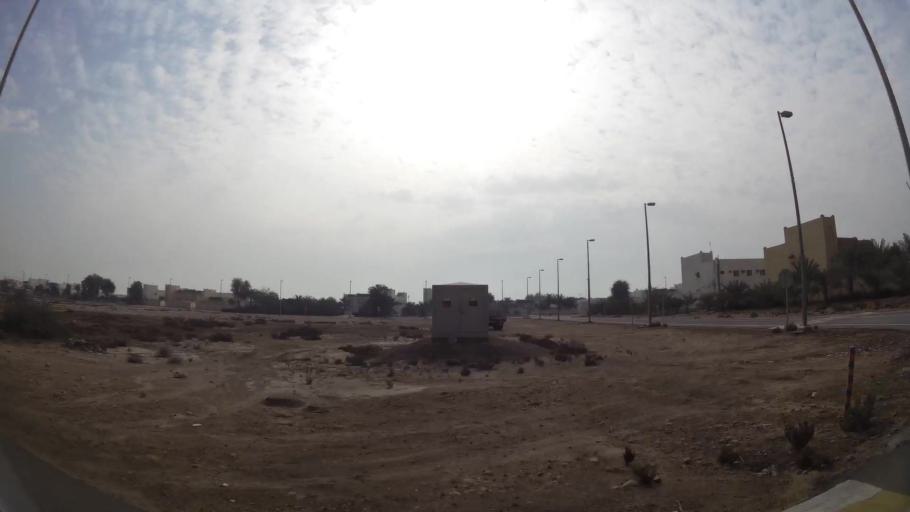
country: AE
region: Abu Dhabi
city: Abu Dhabi
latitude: 24.6653
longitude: 54.7635
